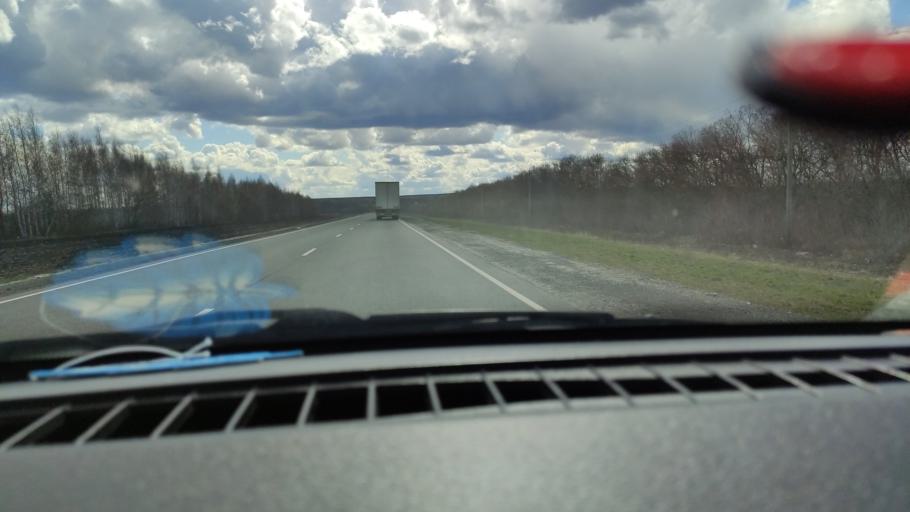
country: RU
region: Samara
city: Varlamovo
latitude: 52.9781
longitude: 48.3108
